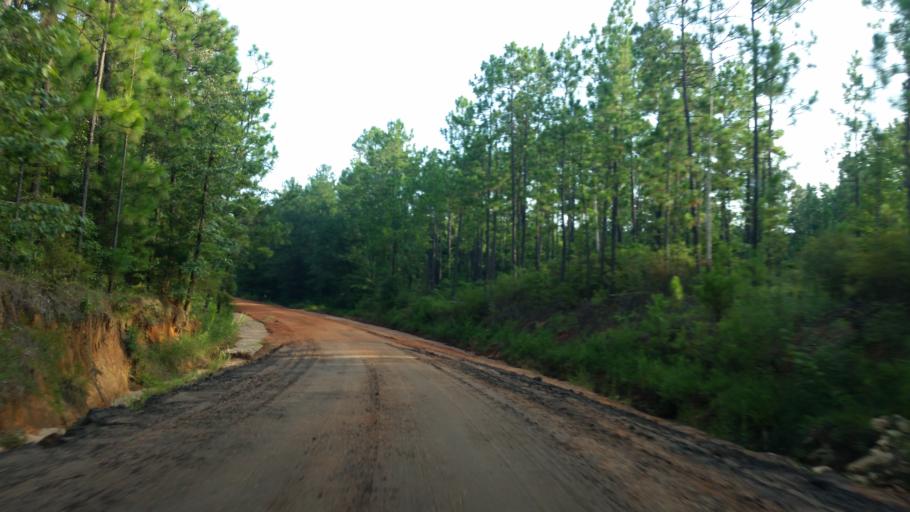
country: US
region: Alabama
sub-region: Escambia County
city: Atmore
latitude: 30.9546
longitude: -87.5718
